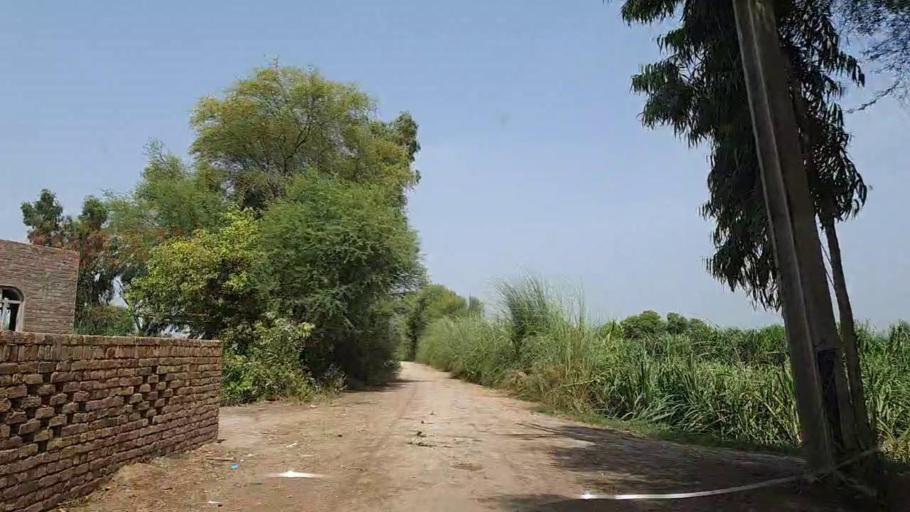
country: PK
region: Sindh
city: Ghotki
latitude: 28.0681
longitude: 69.3160
